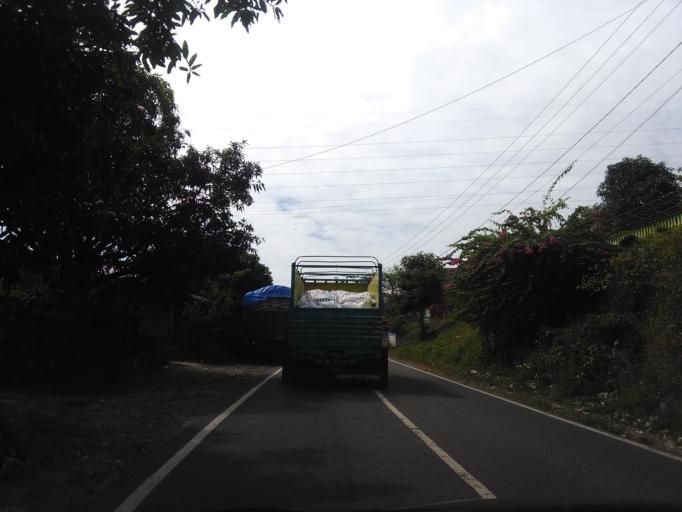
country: ID
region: South Sulawesi
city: Harapankarya
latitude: -3.9738
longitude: 119.6383
